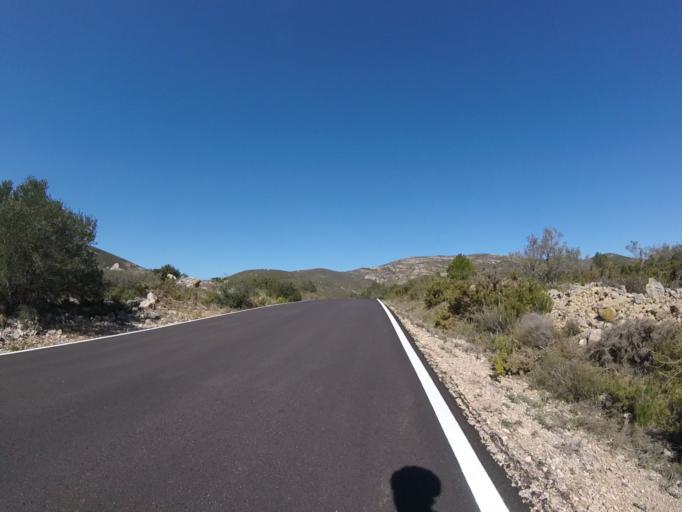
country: ES
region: Valencia
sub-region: Provincia de Castello
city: Cervera del Maestre
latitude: 40.4019
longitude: 0.2308
